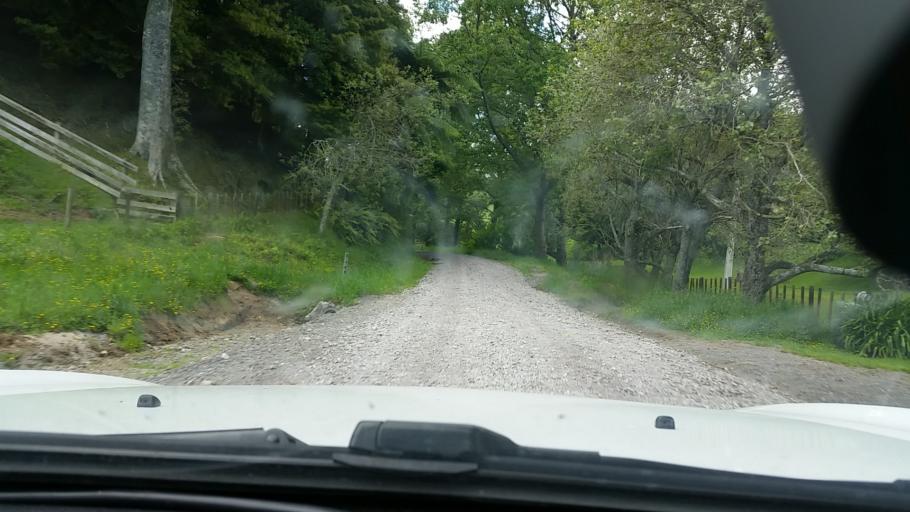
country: NZ
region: Bay of Plenty
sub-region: Western Bay of Plenty District
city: Maketu
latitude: -37.9812
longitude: 176.4035
